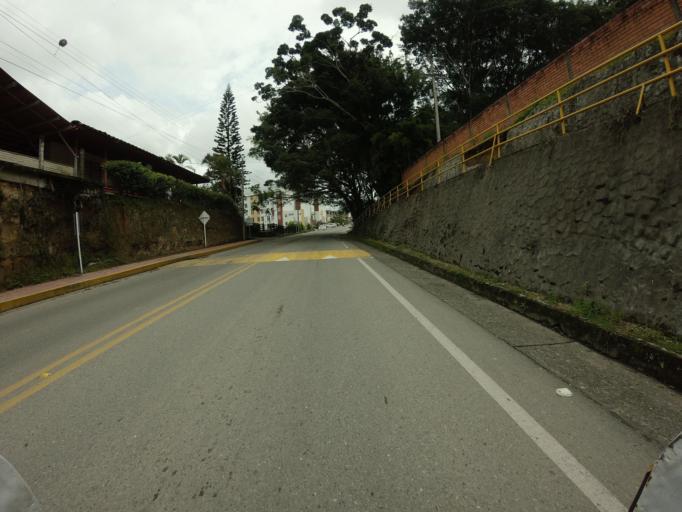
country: CO
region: Quindio
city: Quimbaya
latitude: 4.6284
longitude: -75.7692
